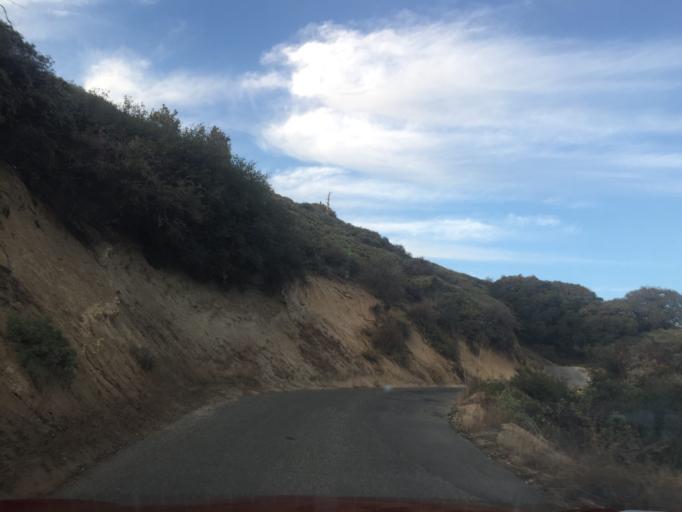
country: US
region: California
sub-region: Tulare County
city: Three Rivers
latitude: 36.4386
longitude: -118.7203
